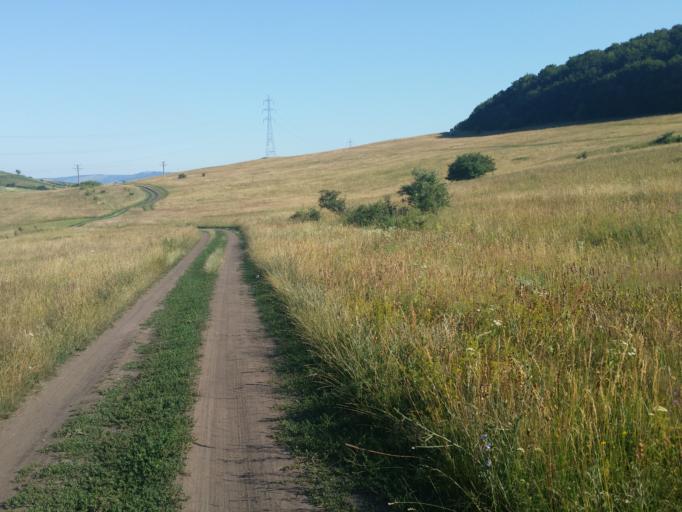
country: RO
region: Cluj
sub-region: Comuna Baciu
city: Baciu
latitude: 46.8070
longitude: 23.5266
